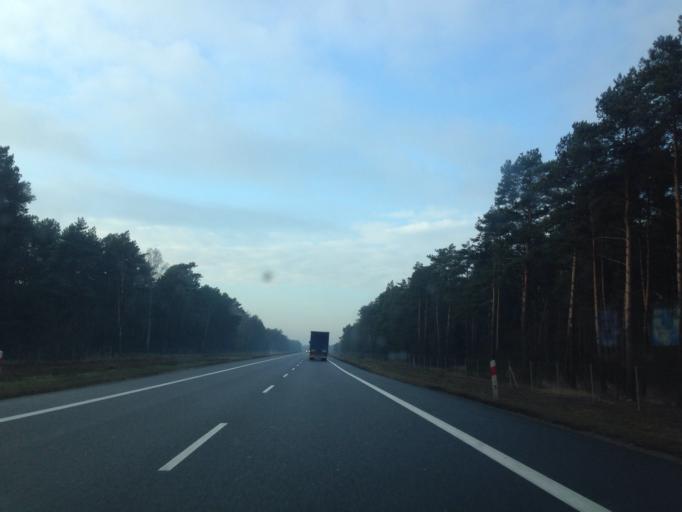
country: PL
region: Kujawsko-Pomorskie
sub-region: Torun
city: Torun
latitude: 52.9744
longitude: 18.6413
